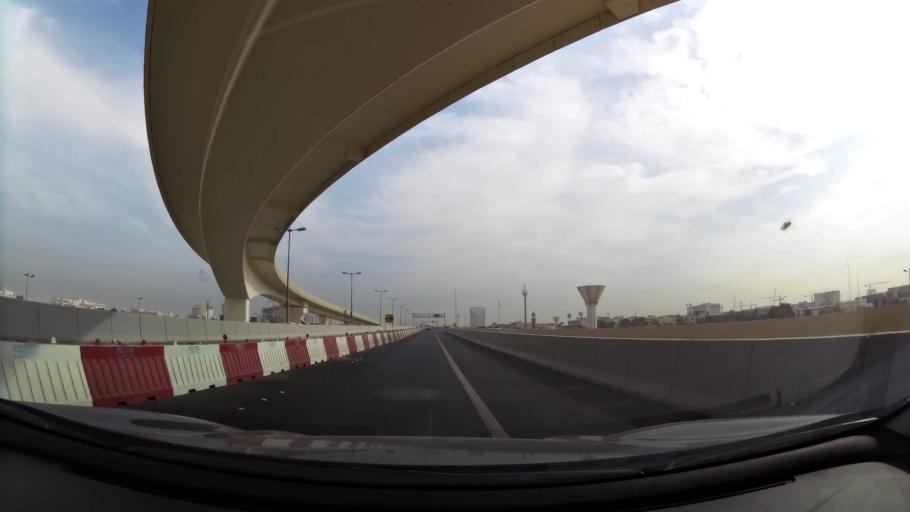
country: KW
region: Al Asimah
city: Ar Rabiyah
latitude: 29.3260
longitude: 47.8958
